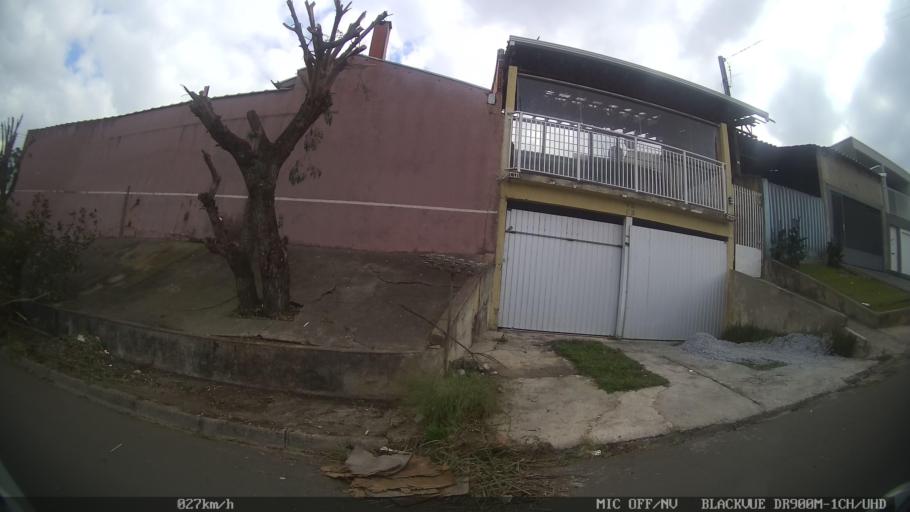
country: BR
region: Parana
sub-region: Colombo
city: Colombo
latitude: -25.3580
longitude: -49.2092
